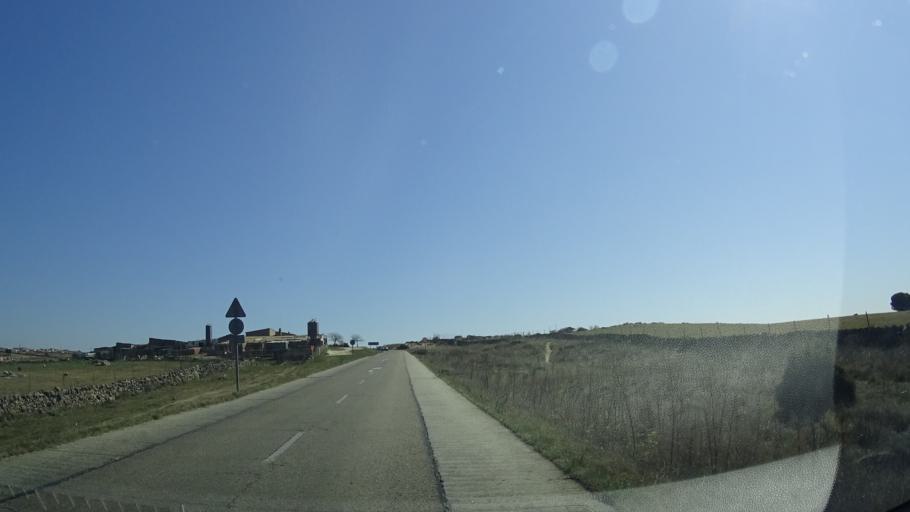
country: ES
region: Madrid
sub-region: Provincia de Madrid
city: Colmenar Viejo
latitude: 40.6483
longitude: -3.8012
